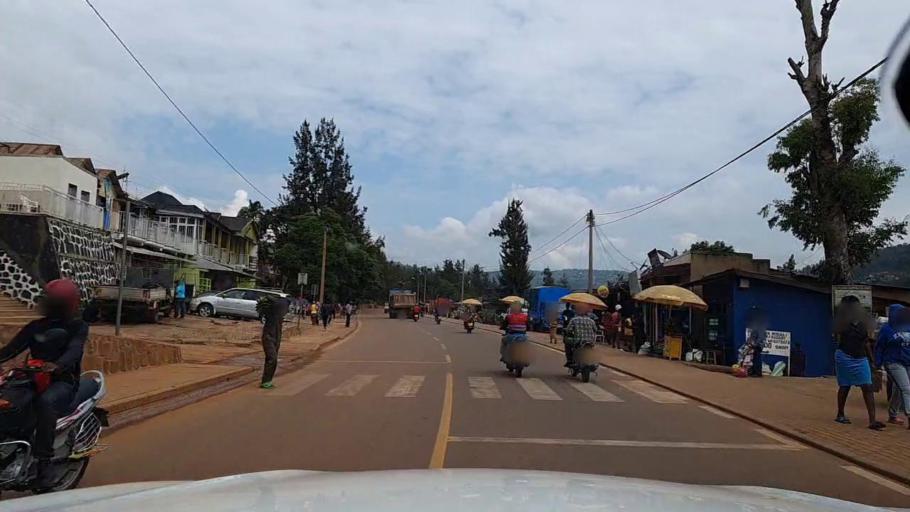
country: RW
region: Kigali
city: Kigali
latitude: -1.9269
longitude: 30.0465
